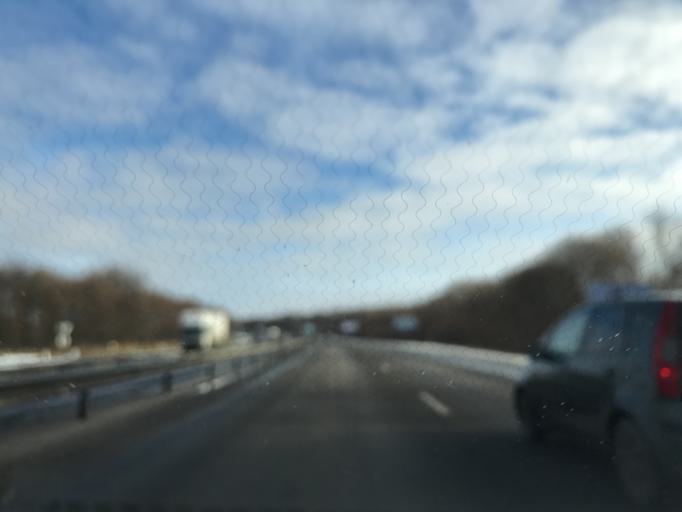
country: RU
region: Rostov
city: Grushevskaya
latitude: 47.3983
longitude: 39.9513
